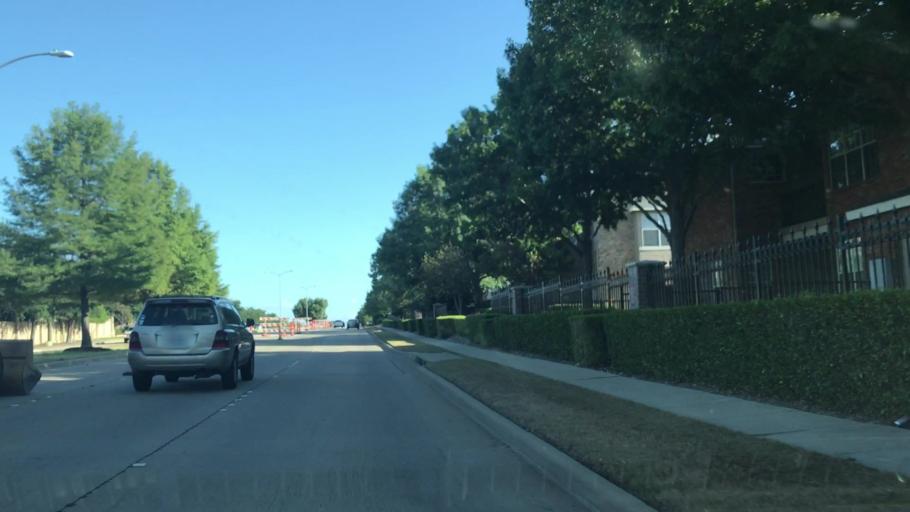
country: US
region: Texas
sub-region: Collin County
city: Allen
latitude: 33.1101
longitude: -96.7336
